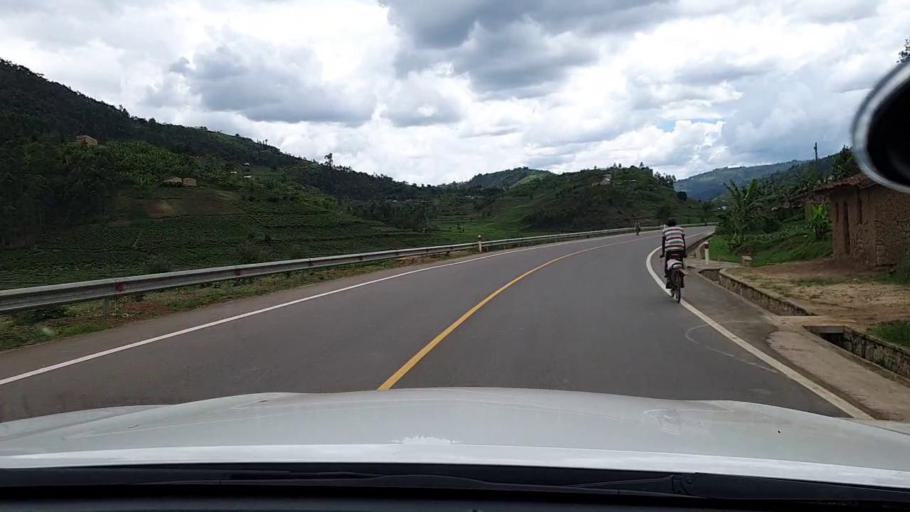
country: RW
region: Northern Province
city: Byumba
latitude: -1.6461
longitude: 29.9008
